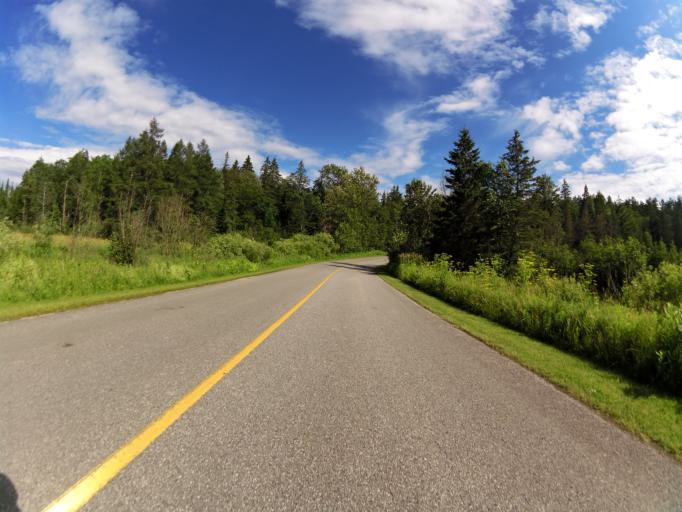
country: CA
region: Quebec
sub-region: Outaouais
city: Wakefield
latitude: 45.6238
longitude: -76.0097
